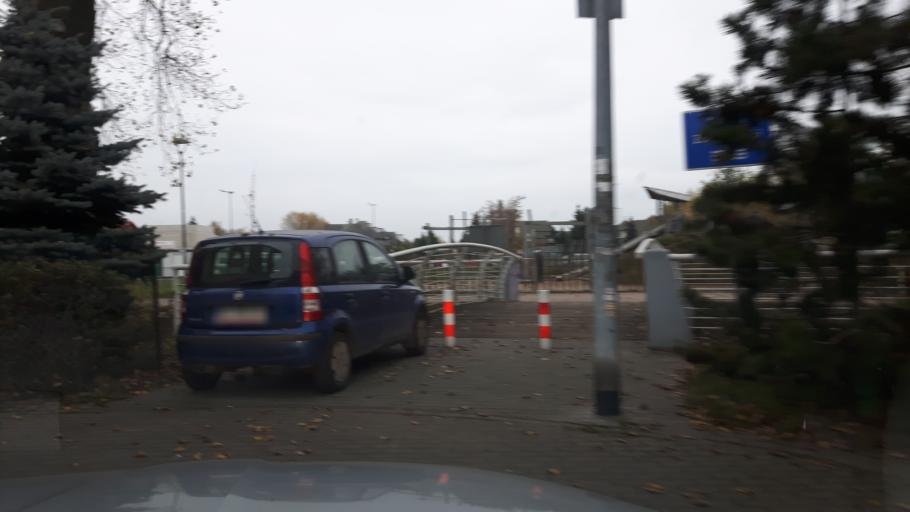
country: PL
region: Masovian Voivodeship
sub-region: Warszawa
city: Targowek
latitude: 52.2902
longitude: 21.0572
